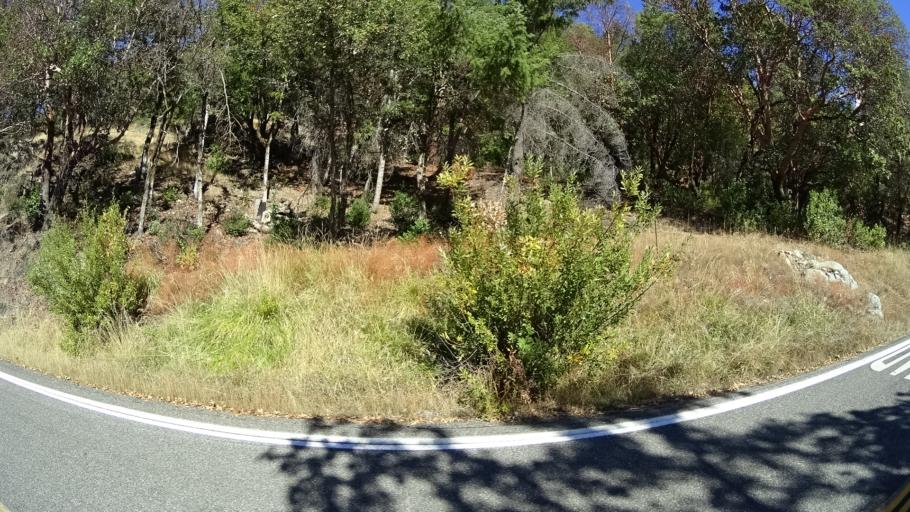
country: US
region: California
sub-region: Siskiyou County
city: Happy Camp
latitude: 41.3813
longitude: -123.4890
